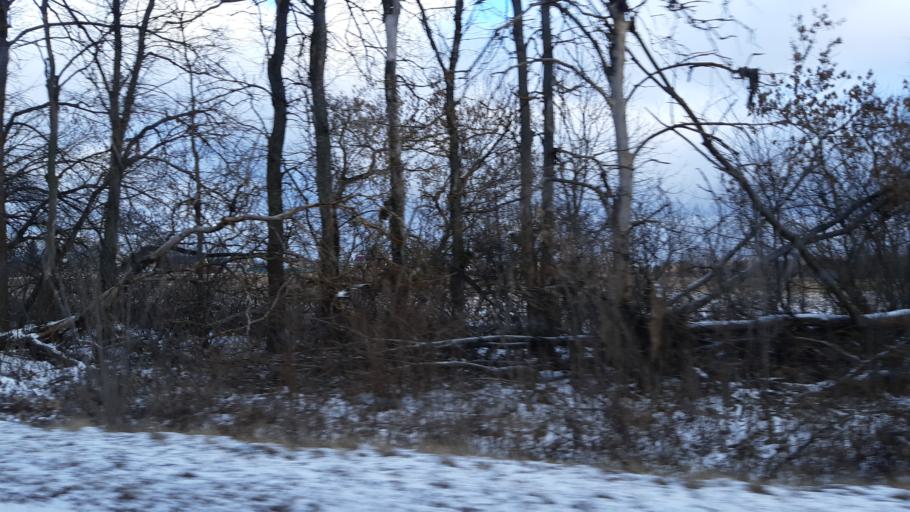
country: RU
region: Moskovskaya
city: Noginsk-9
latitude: 56.0122
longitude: 38.5586
